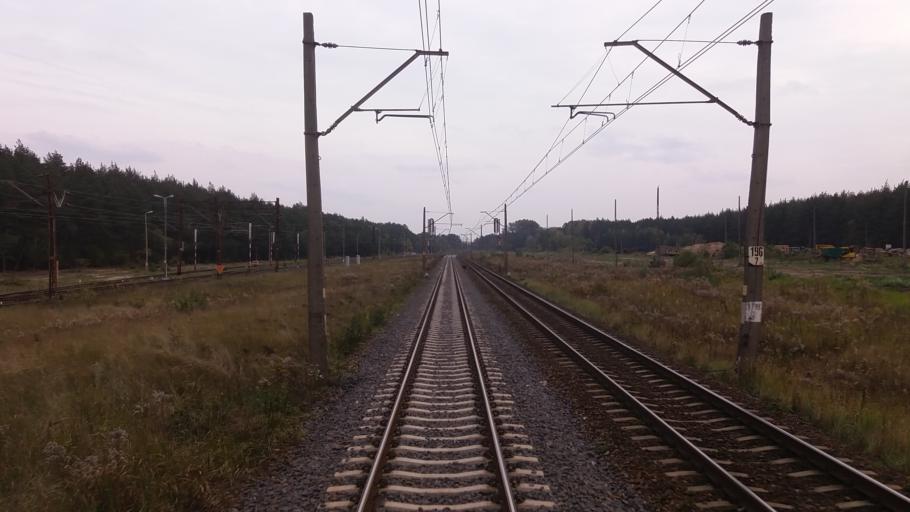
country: PL
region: West Pomeranian Voivodeship
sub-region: Powiat gryfinski
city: Stare Czarnowo
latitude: 53.3905
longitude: 14.6977
